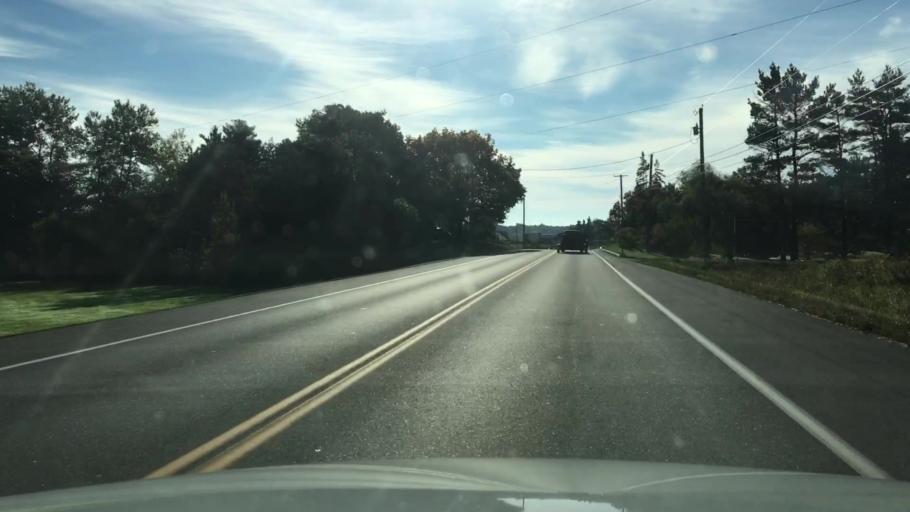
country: US
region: Maine
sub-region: Knox County
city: Warren
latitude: 44.0854
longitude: -69.2300
